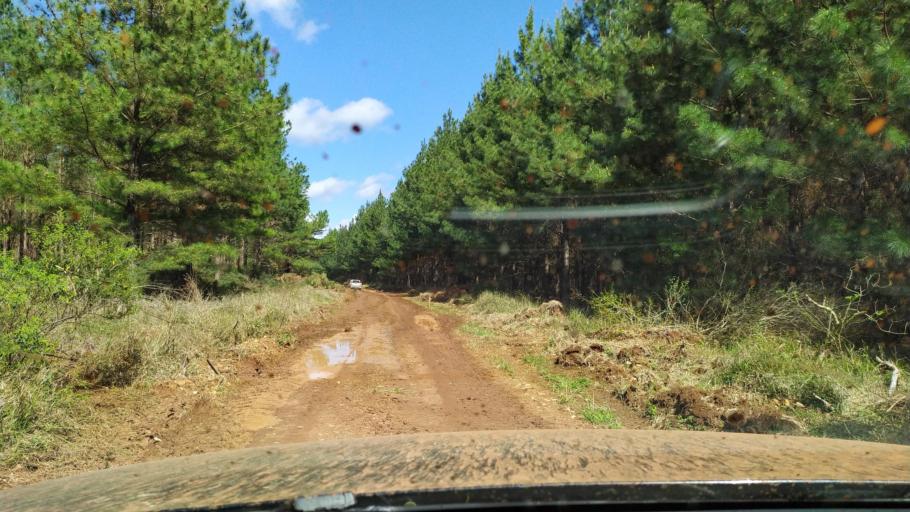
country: AR
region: Corrientes
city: Santo Tome
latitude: -28.4047
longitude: -56.0142
